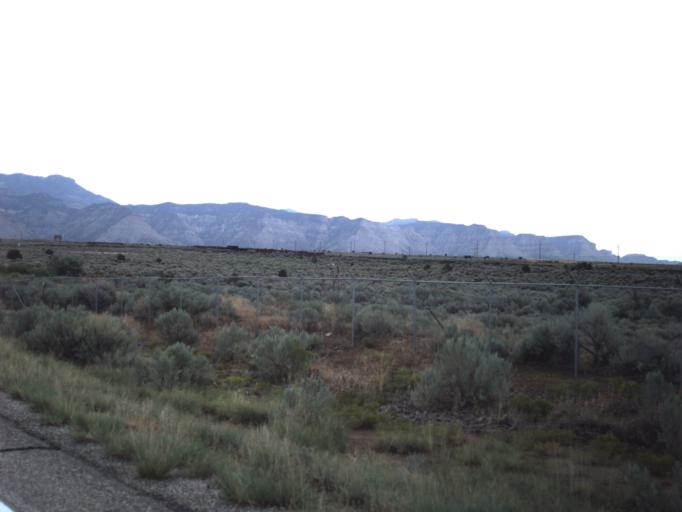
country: US
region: Utah
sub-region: Carbon County
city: East Carbon City
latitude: 39.5356
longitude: -110.4672
